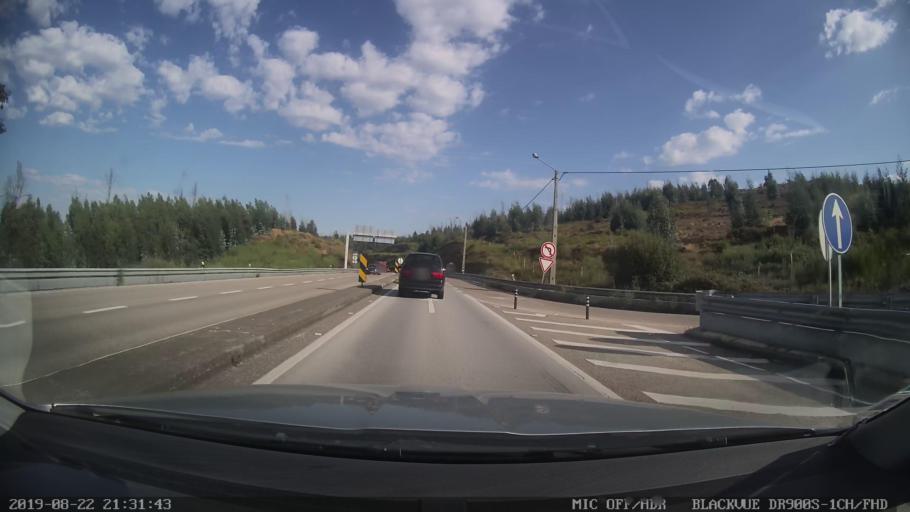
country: PT
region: Leiria
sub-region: Pedrogao Grande
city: Pedrogao Grande
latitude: 39.9232
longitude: -8.1563
